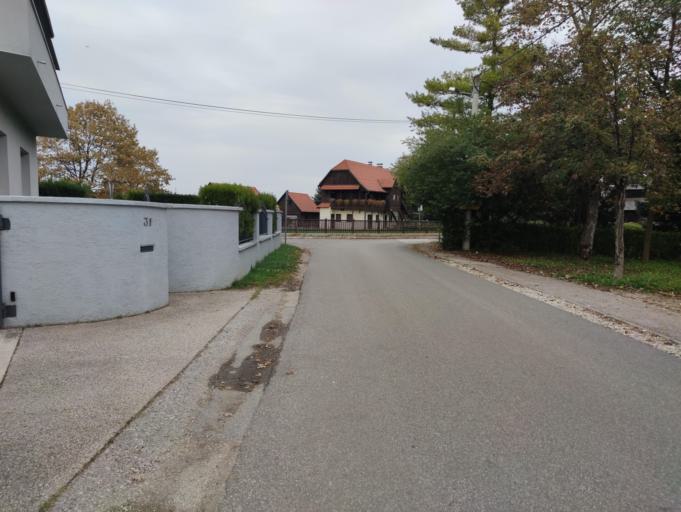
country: HR
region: Grad Zagreb
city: Odra
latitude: 45.7358
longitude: 16.0231
